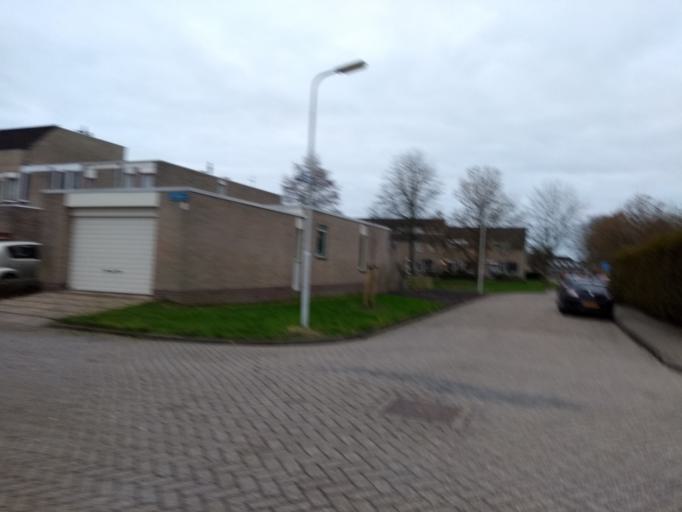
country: NL
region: Friesland
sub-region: Sudwest Fryslan
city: Sneek
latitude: 53.0204
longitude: 5.6456
